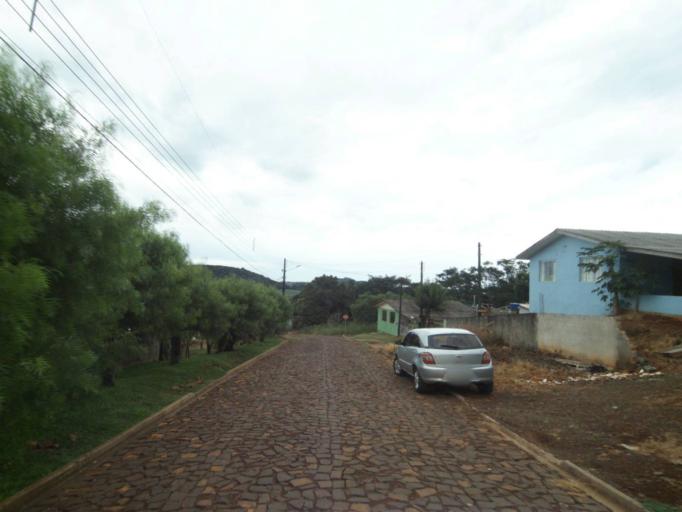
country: BR
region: Parana
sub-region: Guaraniacu
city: Guaraniacu
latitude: -25.1048
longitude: -52.8613
